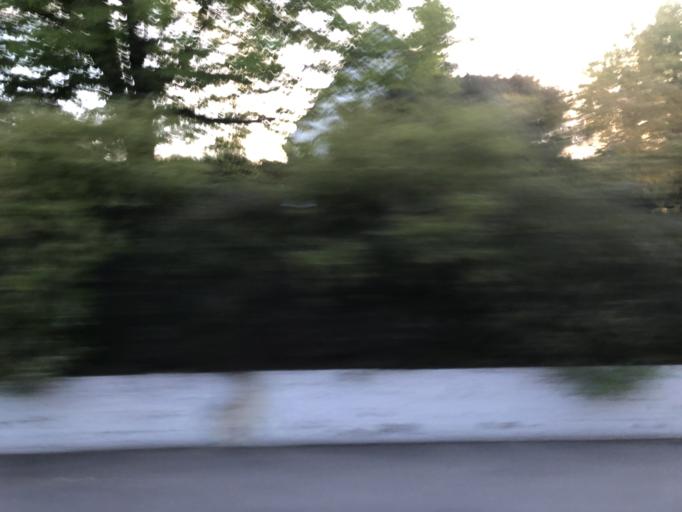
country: DE
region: Baden-Wuerttemberg
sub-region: Tuebingen Region
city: Sickenhausen
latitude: 48.5305
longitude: 9.2040
